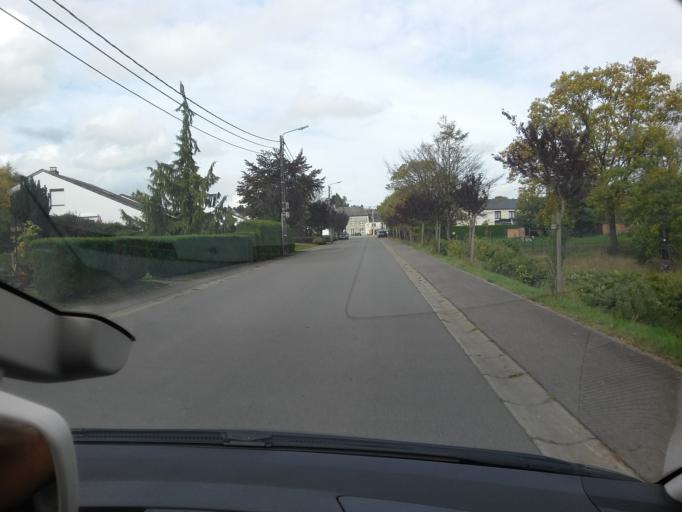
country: BE
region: Wallonia
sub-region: Province du Luxembourg
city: Arlon
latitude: 49.6946
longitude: 5.7675
